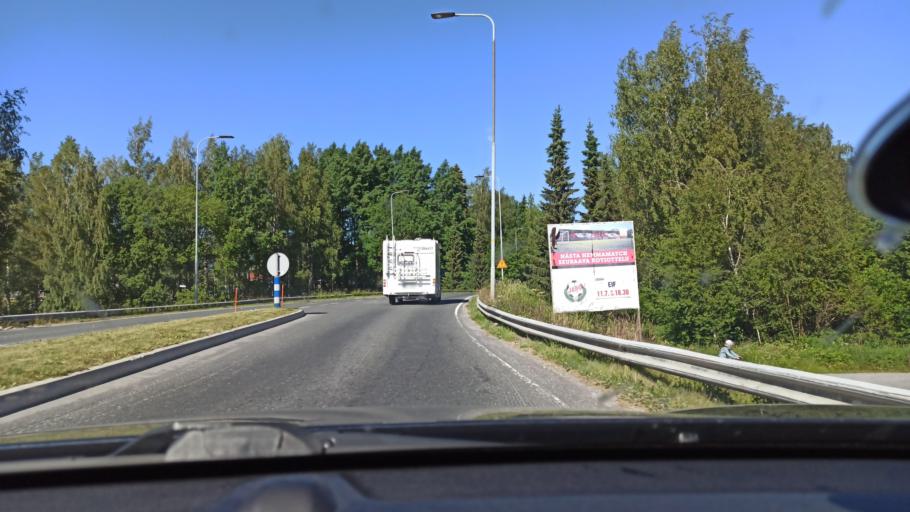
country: FI
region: Ostrobothnia
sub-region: Jakobstadsregionen
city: Jakobstad
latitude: 63.6671
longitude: 22.7073
